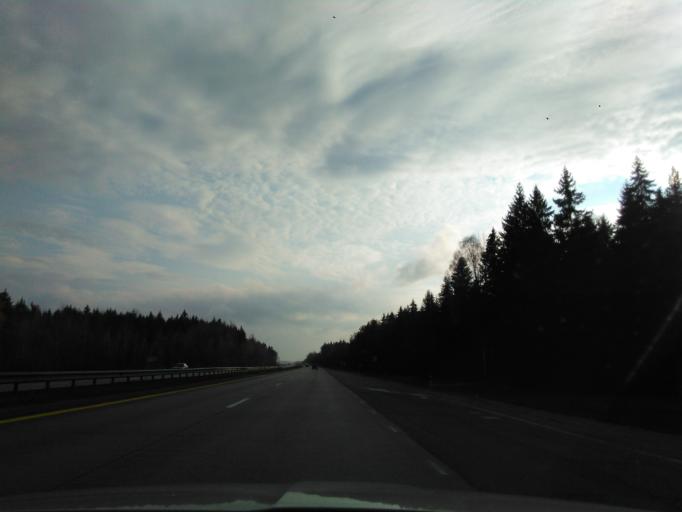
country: BY
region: Minsk
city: Astrashytski Haradok
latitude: 54.0916
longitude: 27.7704
